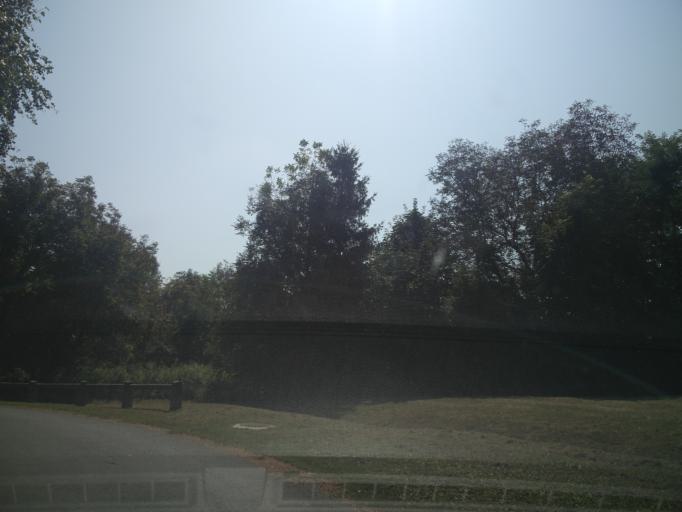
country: HU
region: Zala
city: Zalaegerszeg
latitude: 46.8377
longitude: 16.8605
